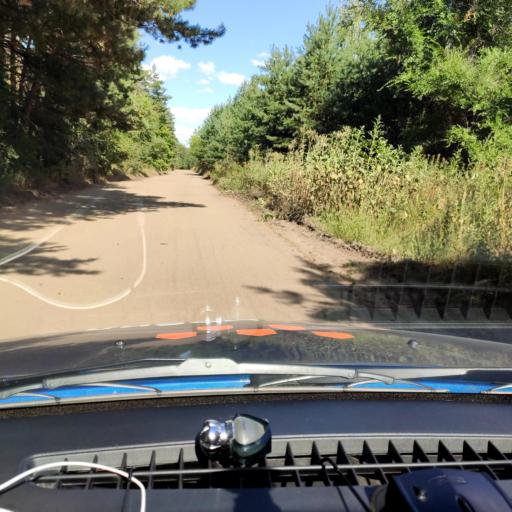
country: RU
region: Voronezj
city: Somovo
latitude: 51.7189
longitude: 39.3850
